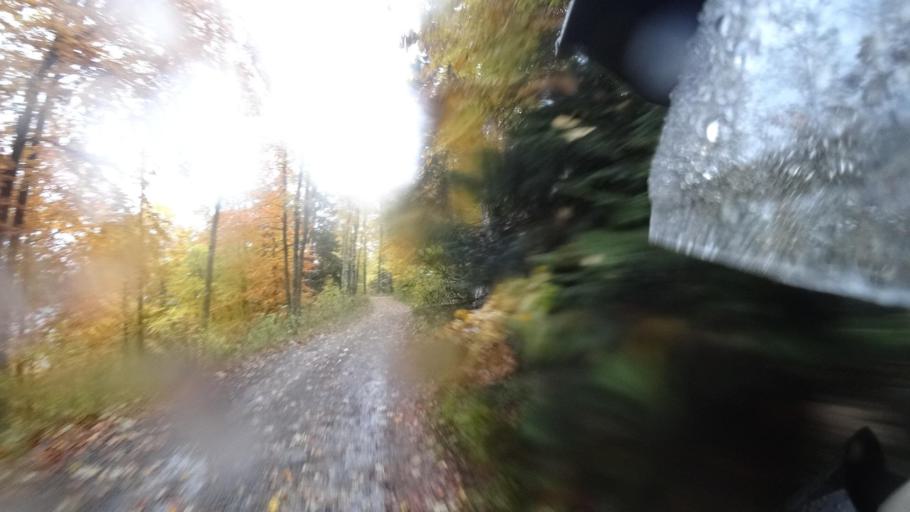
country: HR
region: Primorsko-Goranska
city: Vrbovsko
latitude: 45.3096
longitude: 15.0742
